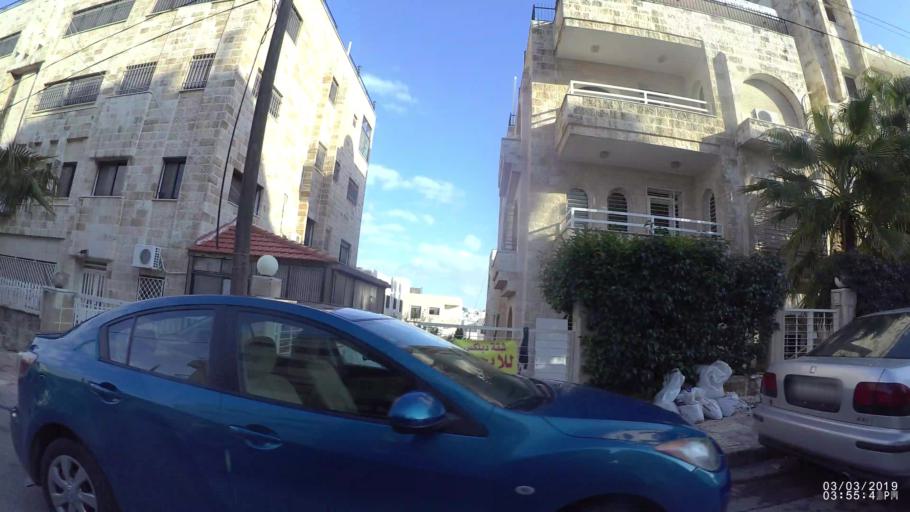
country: JO
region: Amman
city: Al Jubayhah
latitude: 31.9828
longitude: 35.8703
